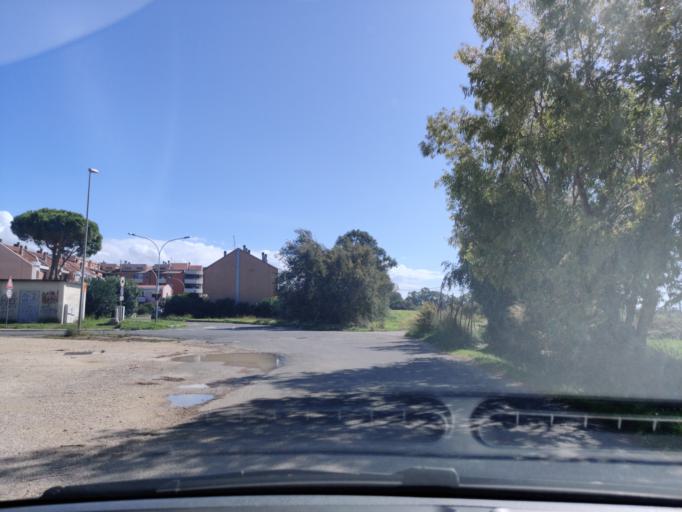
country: IT
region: Latium
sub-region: Citta metropolitana di Roma Capitale
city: Aurelia
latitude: 42.1365
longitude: 11.7828
